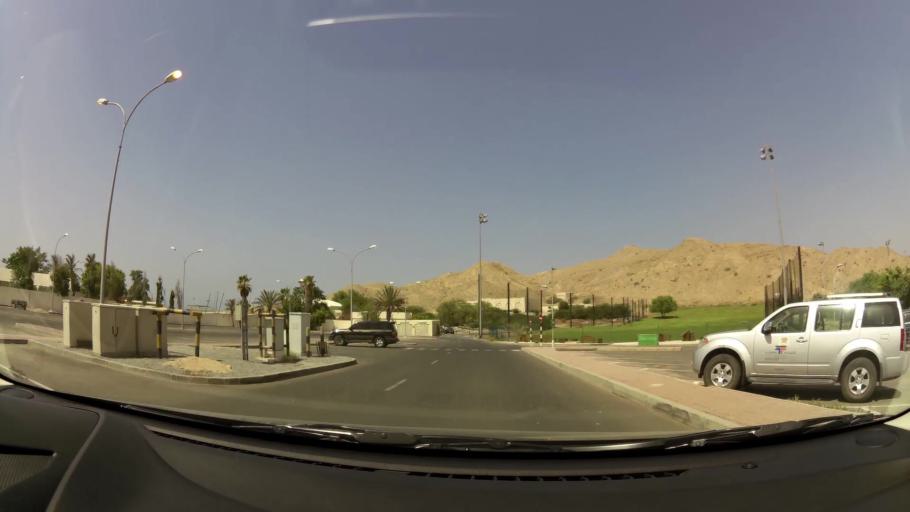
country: OM
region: Muhafazat Masqat
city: Muscat
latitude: 23.6404
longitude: 58.4973
